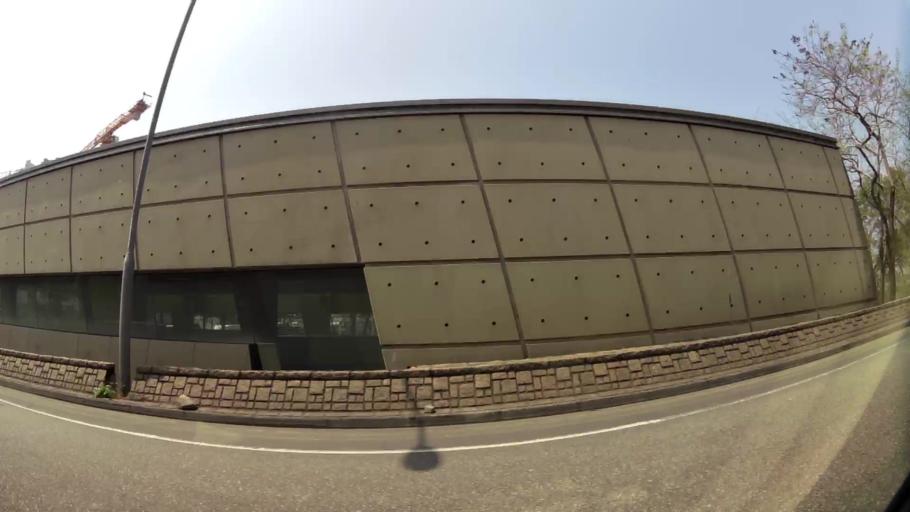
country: HK
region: Sham Shui Po
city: Sham Shui Po
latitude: 22.3253
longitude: 114.1541
